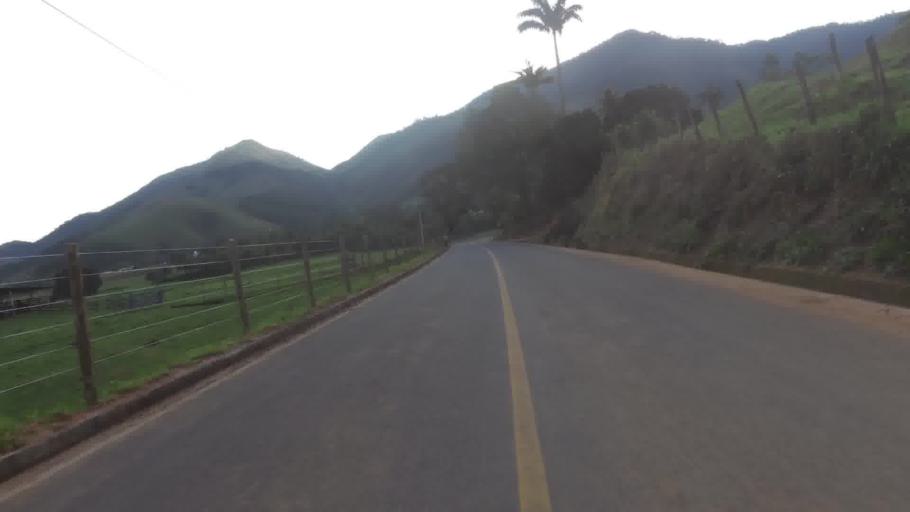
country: BR
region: Espirito Santo
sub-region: Alfredo Chaves
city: Alfredo Chaves
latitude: -20.6024
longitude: -40.7158
